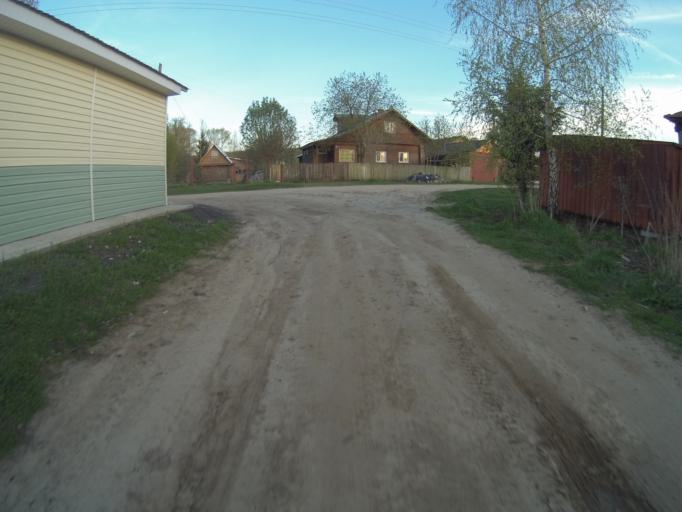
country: RU
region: Vladimir
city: Raduzhnyy
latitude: 56.0281
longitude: 40.2813
